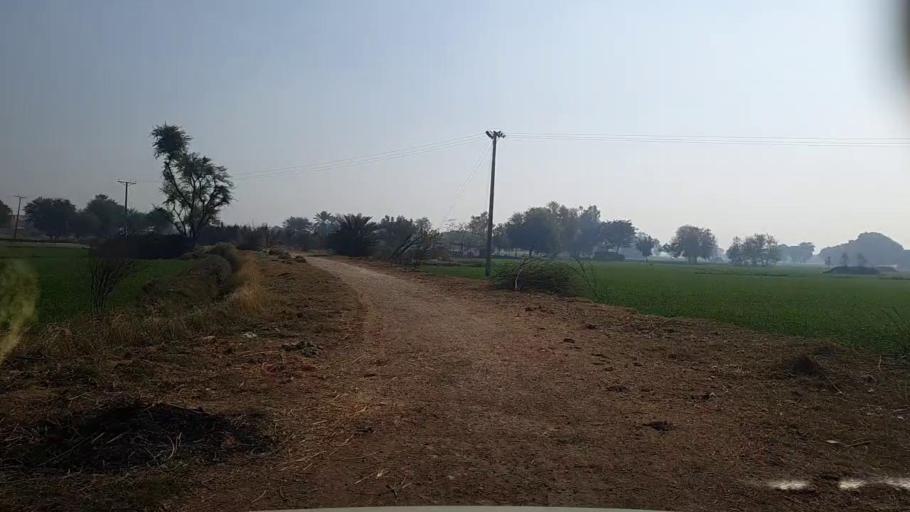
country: PK
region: Sindh
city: Khairpur
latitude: 27.9432
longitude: 69.6749
